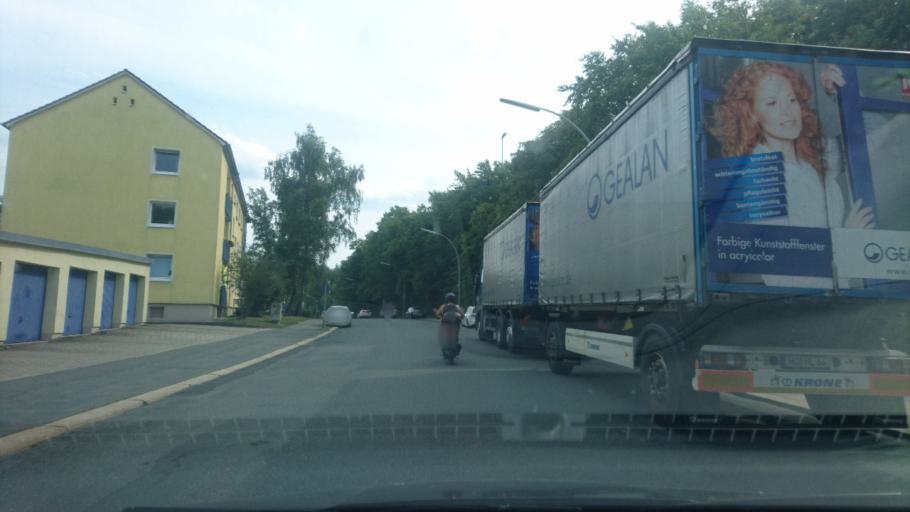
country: DE
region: Bavaria
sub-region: Upper Franconia
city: Hof
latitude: 50.3125
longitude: 11.9009
